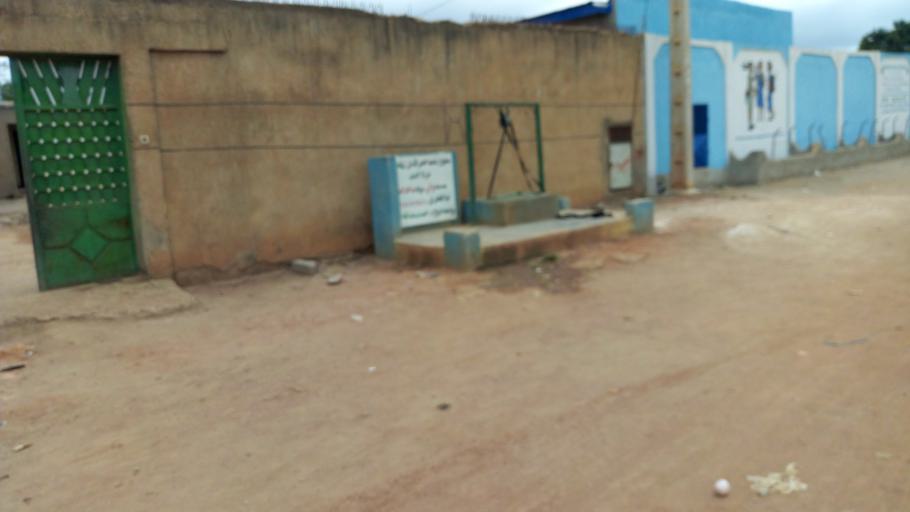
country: CI
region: Vallee du Bandama
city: Bouake
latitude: 7.7268
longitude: -5.0483
